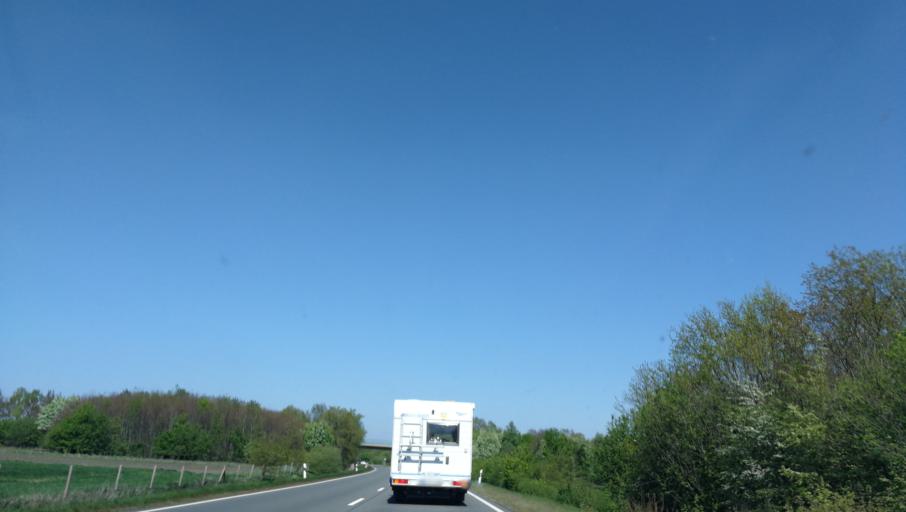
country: DE
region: North Rhine-Westphalia
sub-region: Regierungsbezirk Munster
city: Neuenkirchen
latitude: 52.2399
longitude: 7.4050
